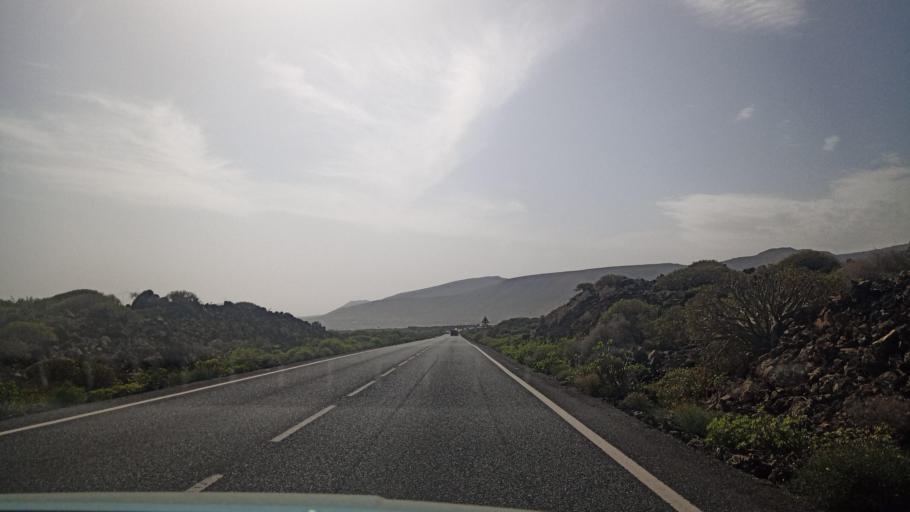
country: ES
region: Canary Islands
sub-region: Provincia de Las Palmas
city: Haria
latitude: 29.1416
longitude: -13.4551
